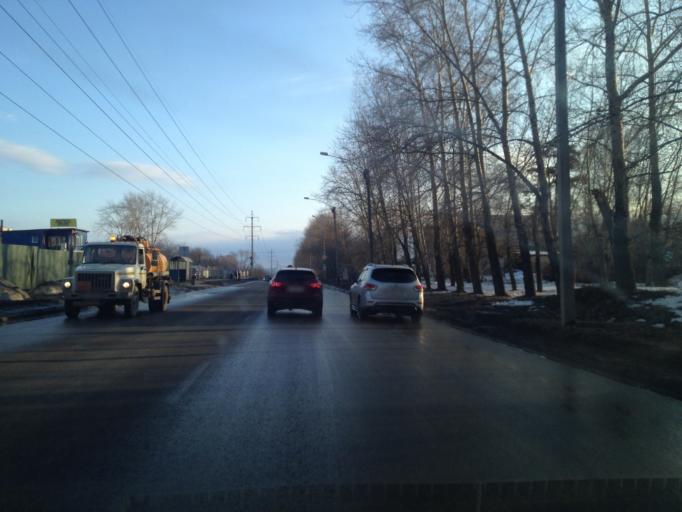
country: RU
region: Sverdlovsk
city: Sovkhoznyy
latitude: 56.7705
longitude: 60.5962
